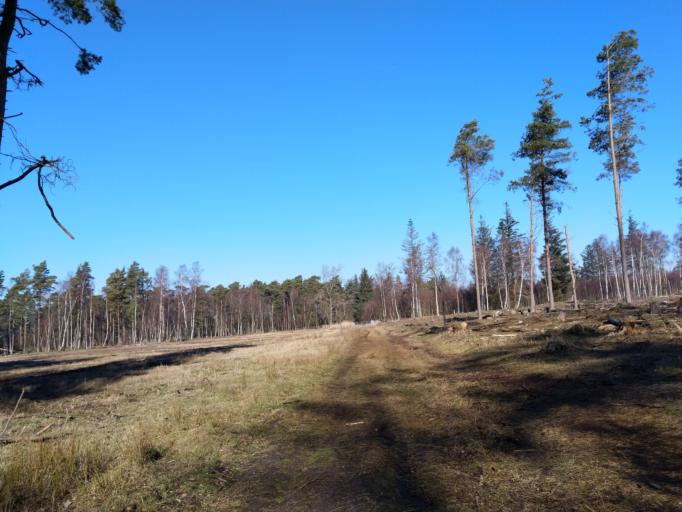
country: DK
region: Zealand
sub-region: Guldborgsund Kommune
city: Nykobing Falster
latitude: 54.6430
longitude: 11.9569
